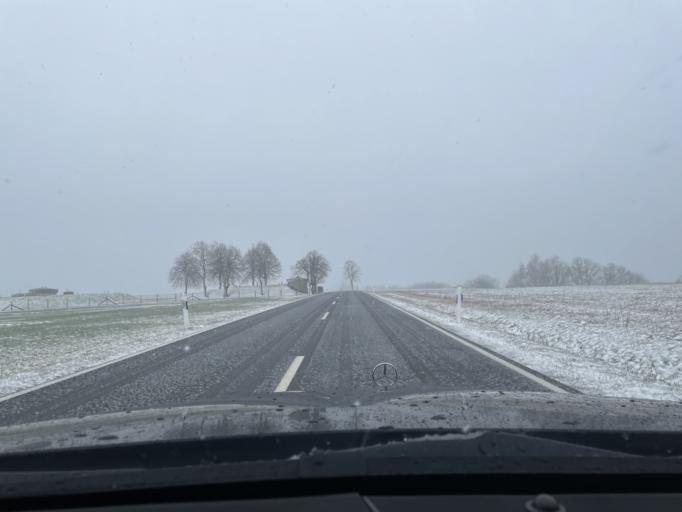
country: DE
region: Thuringia
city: Effelder
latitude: 51.2337
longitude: 10.2733
